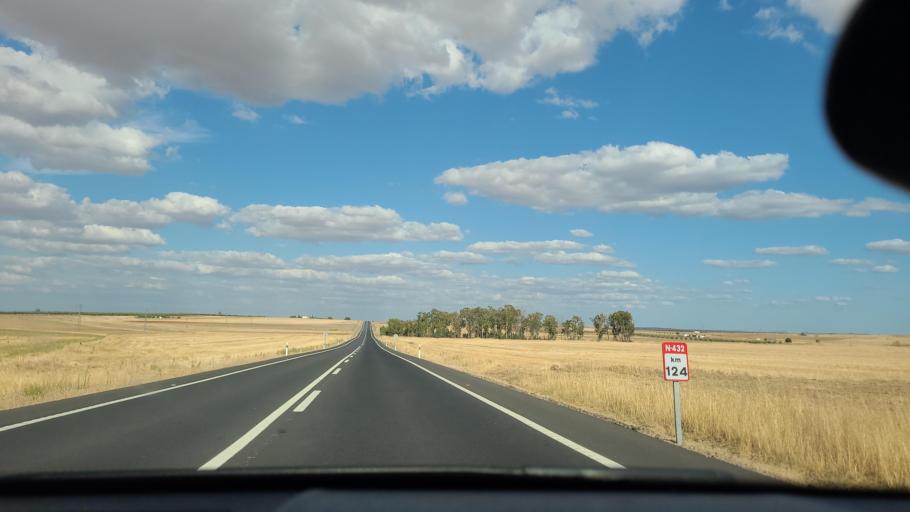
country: ES
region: Extremadura
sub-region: Provincia de Badajoz
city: Ahillones
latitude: 38.2560
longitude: -5.8996
